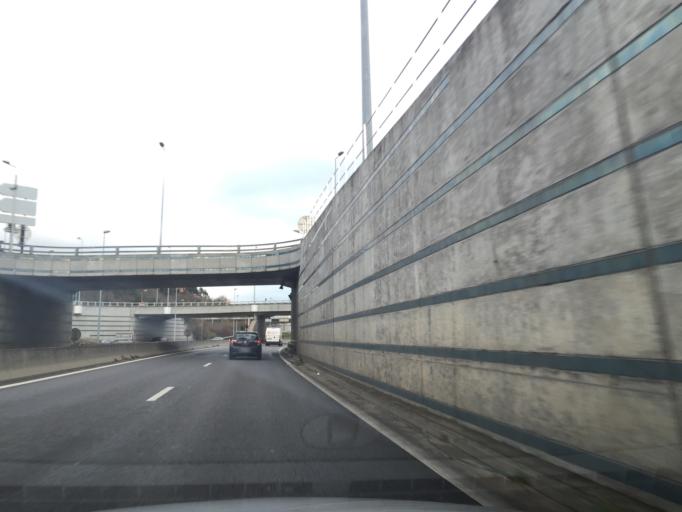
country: FR
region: Rhone-Alpes
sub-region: Departement du Rhone
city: Caluire-et-Cuire
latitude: 45.7907
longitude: 4.8688
